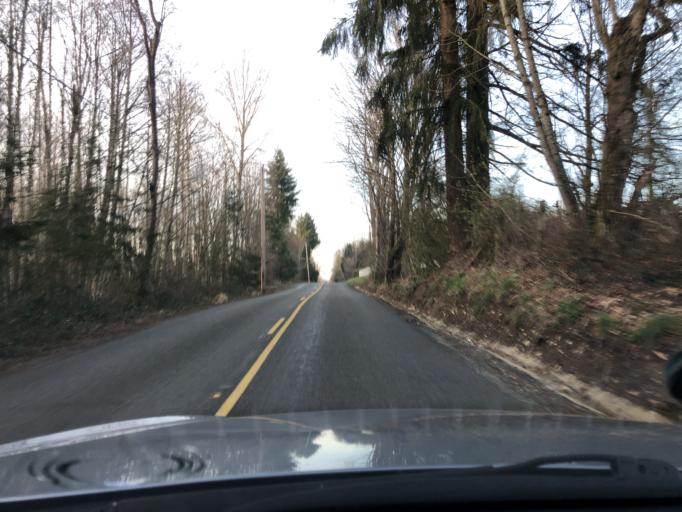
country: US
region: Washington
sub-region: Pierce County
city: Bonney Lake
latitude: 47.2087
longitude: -122.1228
